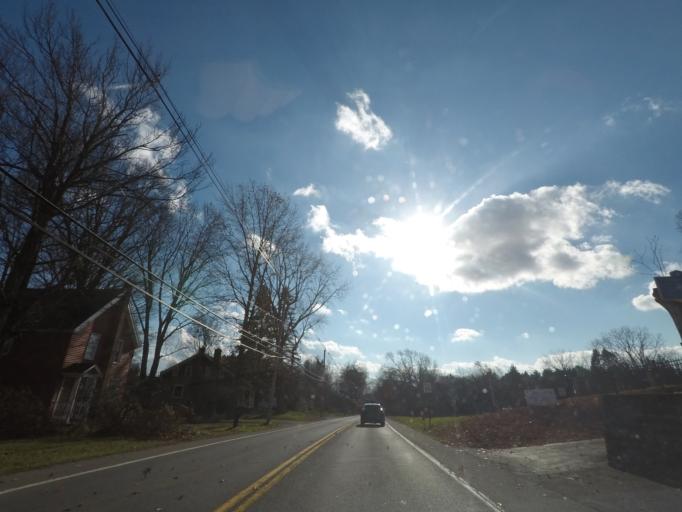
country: US
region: New York
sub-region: Schenectady County
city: East Glenville
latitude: 42.9071
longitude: -73.8959
